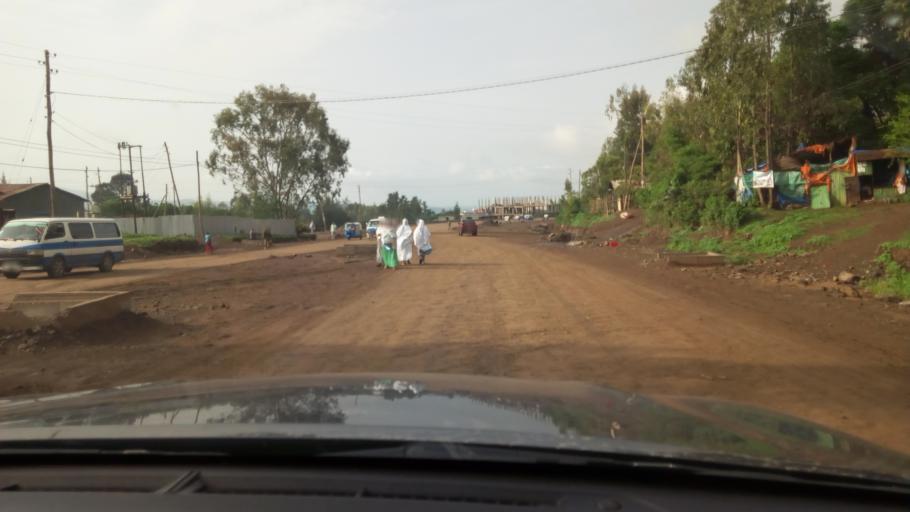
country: ET
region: Amhara
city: Gondar
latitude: 12.5693
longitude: 37.4339
